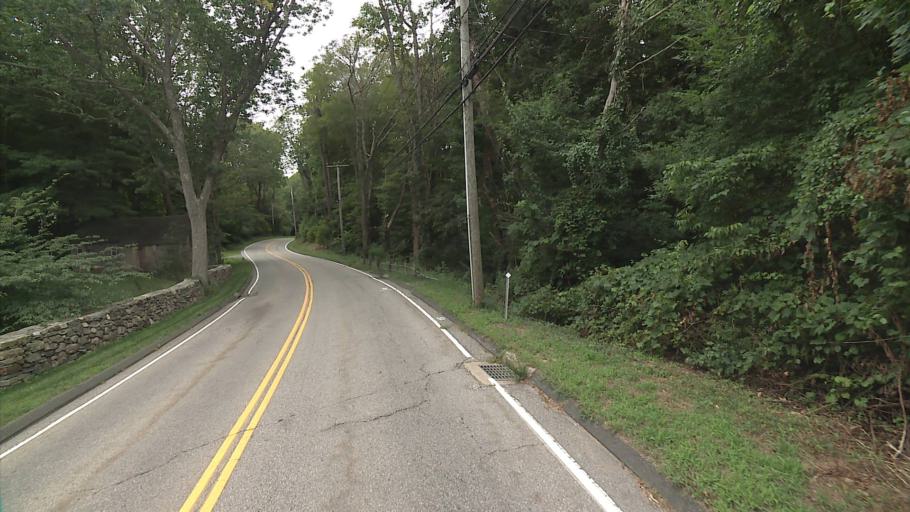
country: US
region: Connecticut
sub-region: Middlesex County
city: Essex Village
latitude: 41.3962
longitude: -72.3456
